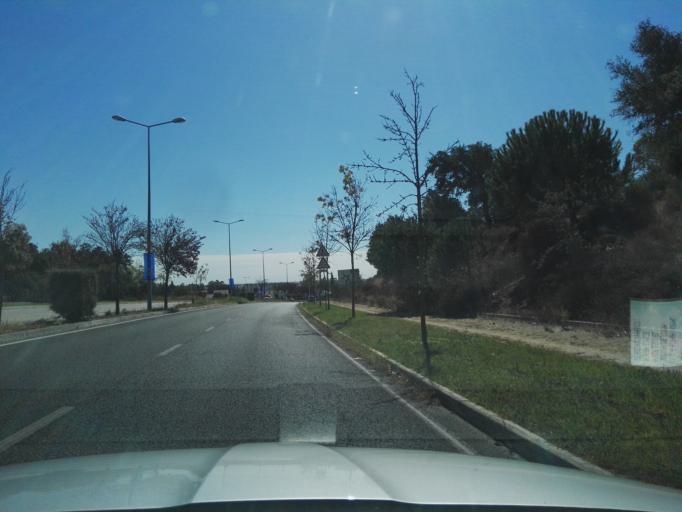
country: PT
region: Setubal
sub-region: Alcochete
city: Alcochete
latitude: 38.7473
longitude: -8.9320
